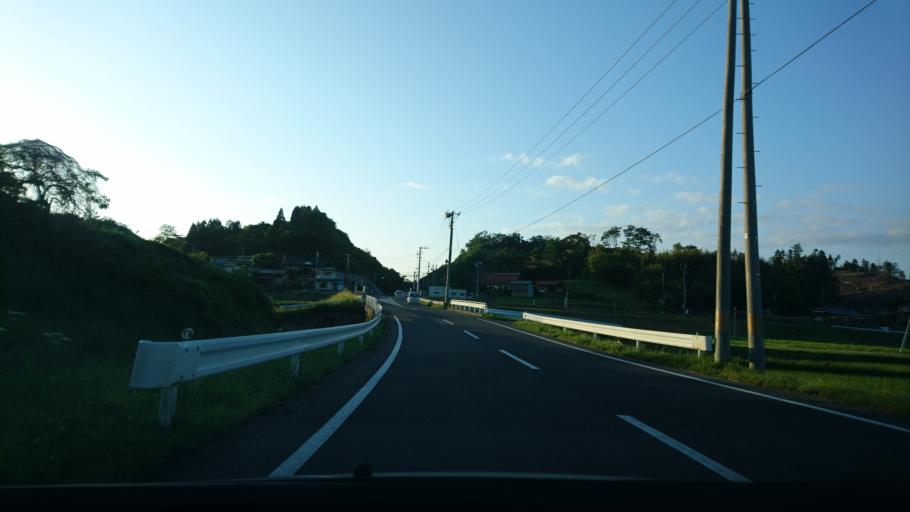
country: JP
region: Iwate
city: Ichinoseki
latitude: 38.8986
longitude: 141.1589
